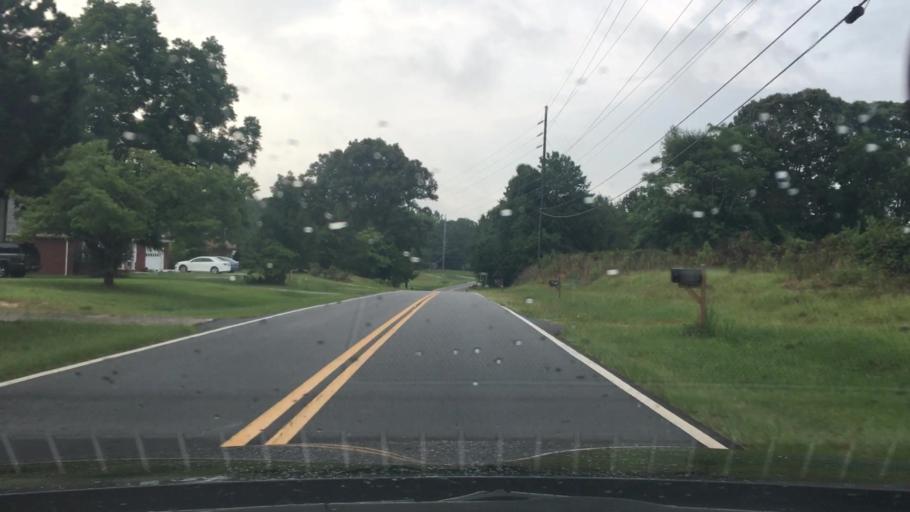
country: US
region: Georgia
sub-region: Spalding County
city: Experiment
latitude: 33.2451
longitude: -84.3849
